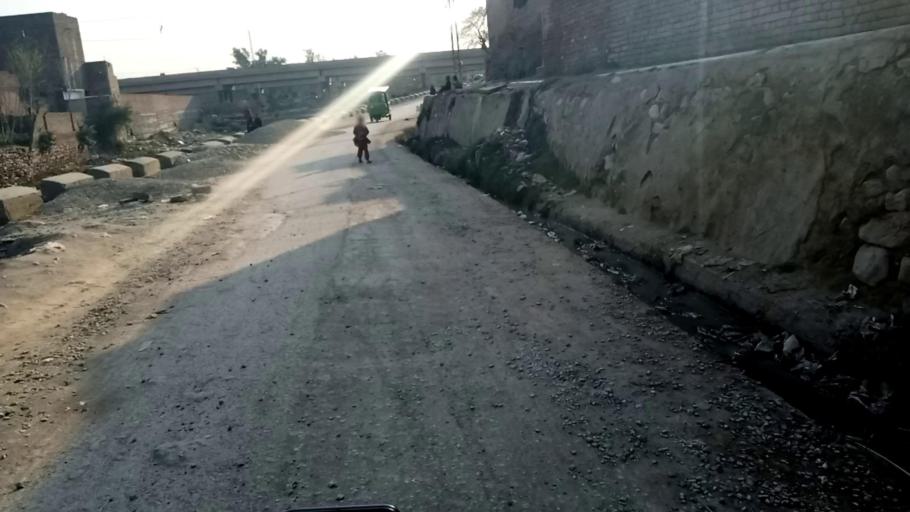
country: PK
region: Khyber Pakhtunkhwa
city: Peshawar
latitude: 34.0051
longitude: 71.4672
